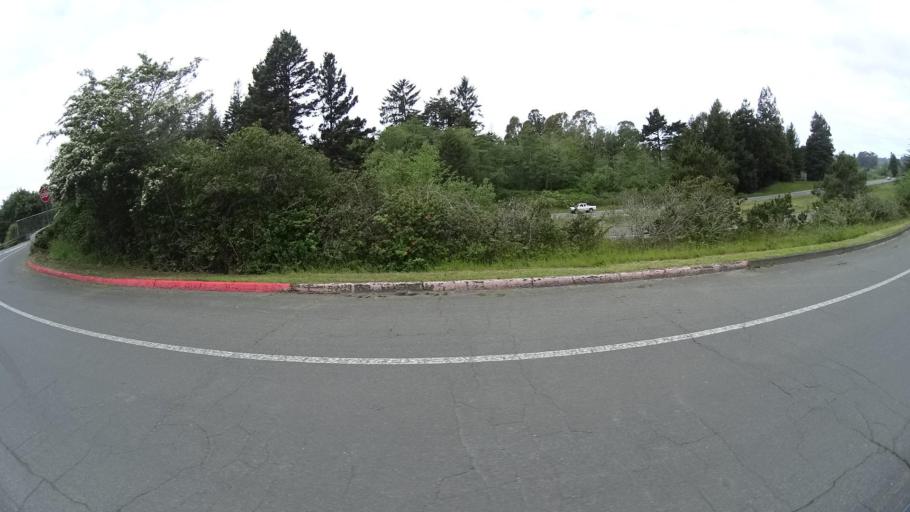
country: US
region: California
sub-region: Humboldt County
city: Arcata
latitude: 40.8862
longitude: -124.0791
